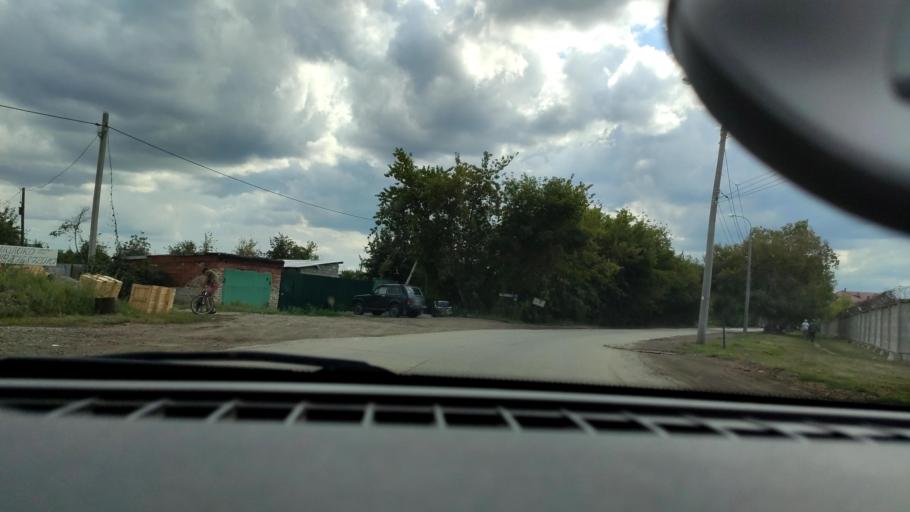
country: RU
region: Samara
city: Novokuybyshevsk
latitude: 53.1074
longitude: 50.0419
